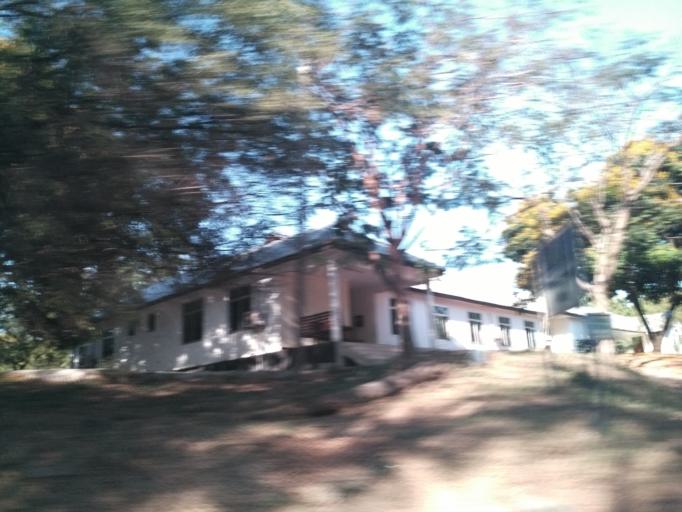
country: TZ
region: Dar es Salaam
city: Magomeni
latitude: -6.7456
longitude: 39.2391
